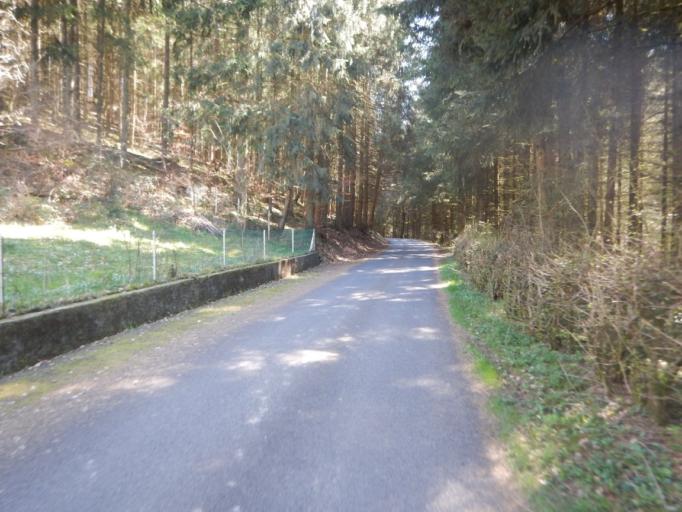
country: LU
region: Diekirch
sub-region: Canton de Clervaux
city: Weiswampach
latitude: 50.1066
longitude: 6.0429
